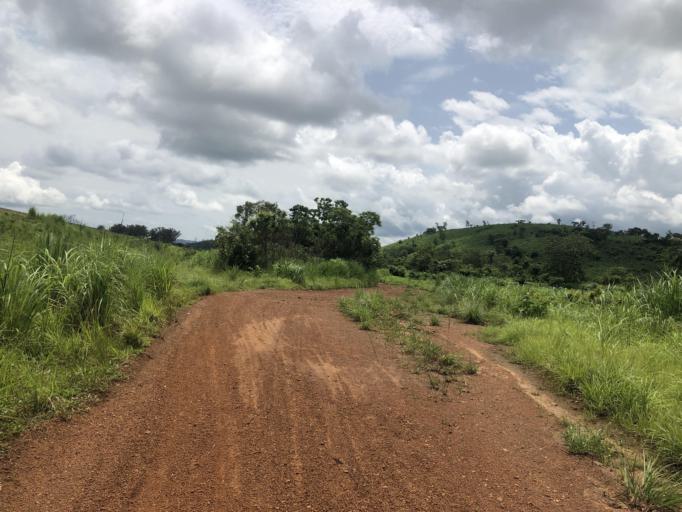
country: SL
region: Northern Province
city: Bumbuna
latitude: 8.9980
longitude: -11.7587
